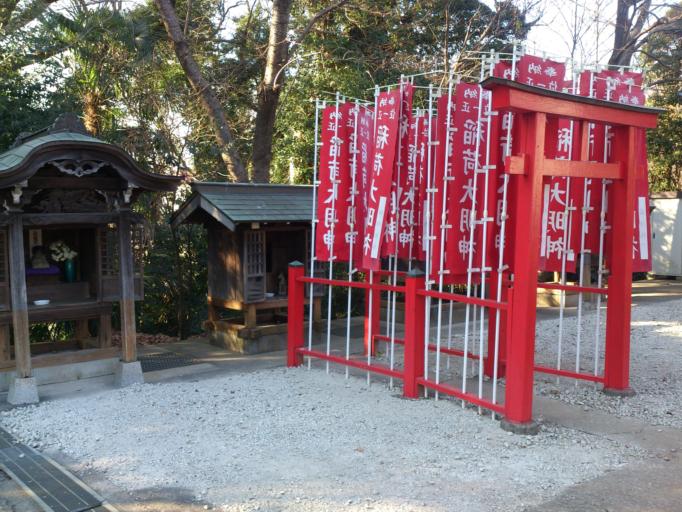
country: JP
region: Chiba
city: Kashiwa
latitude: 35.8057
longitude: 139.9516
